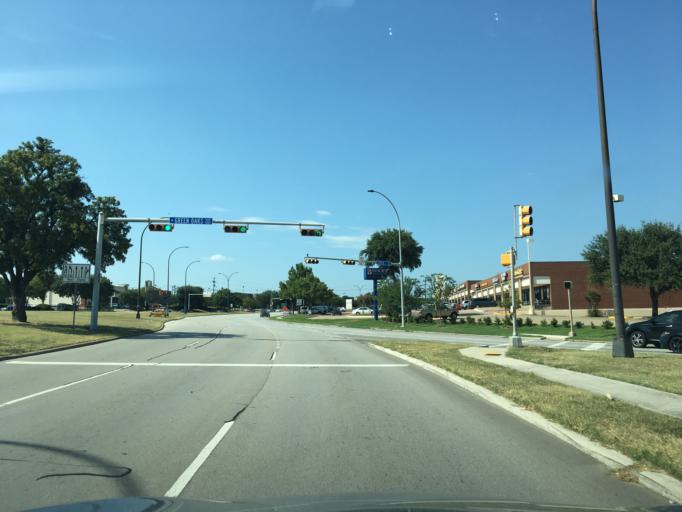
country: US
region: Texas
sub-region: Tarrant County
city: Kennedale
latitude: 32.6792
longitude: -97.1959
